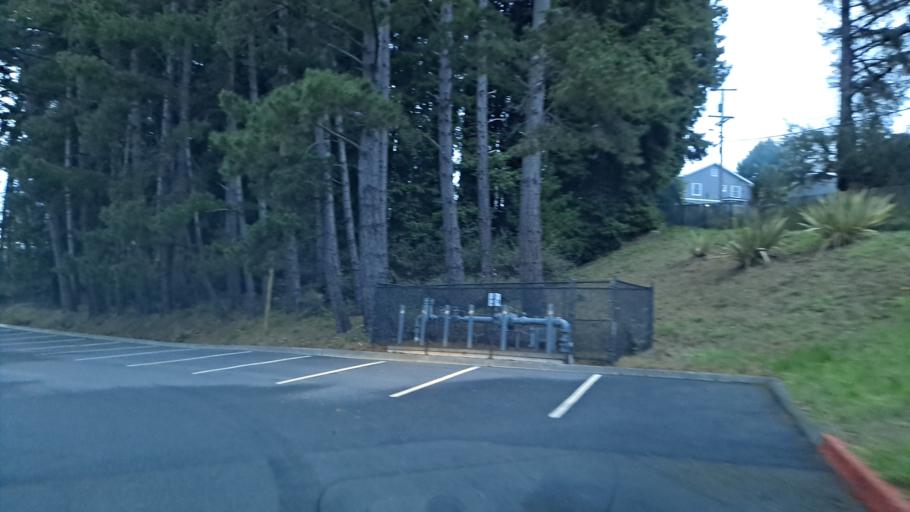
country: US
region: California
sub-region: Humboldt County
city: Arcata
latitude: 40.8715
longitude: -124.0771
